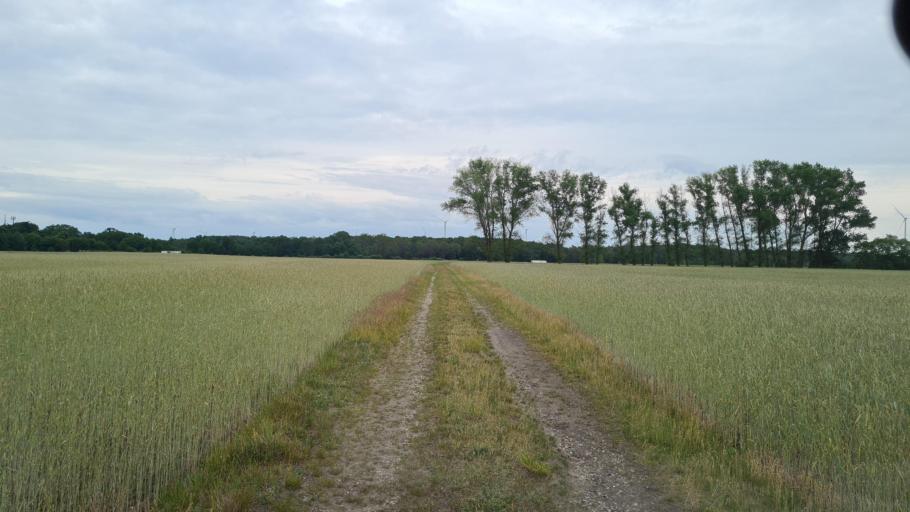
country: DE
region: Brandenburg
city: Bronkow
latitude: 51.6274
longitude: 13.9346
